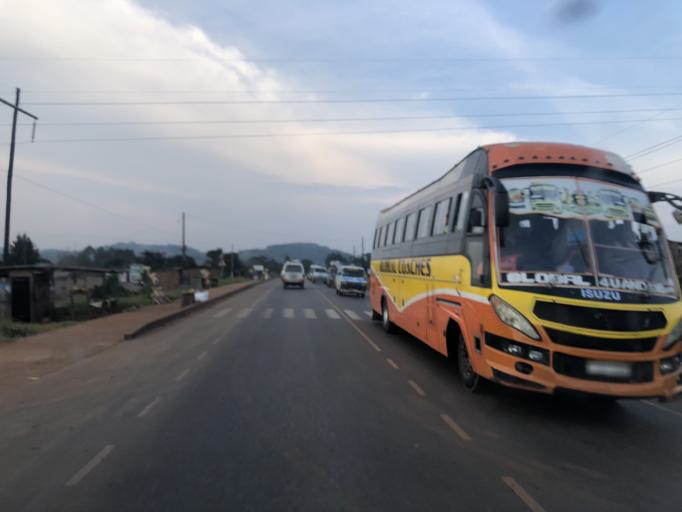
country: UG
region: Central Region
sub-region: Mpigi District
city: Mpigi
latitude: 0.2362
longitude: 32.3477
